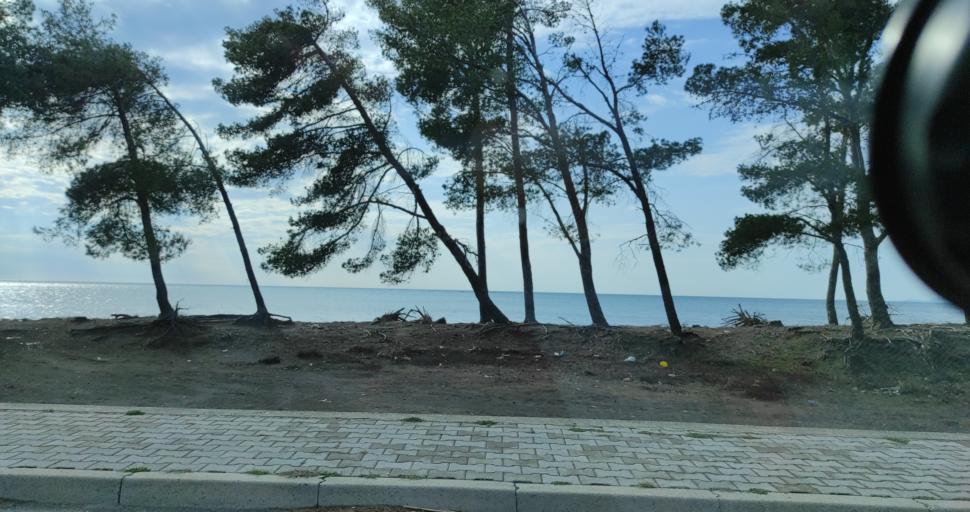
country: AL
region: Lezhe
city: Shengjin
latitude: 41.7883
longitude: 19.6031
